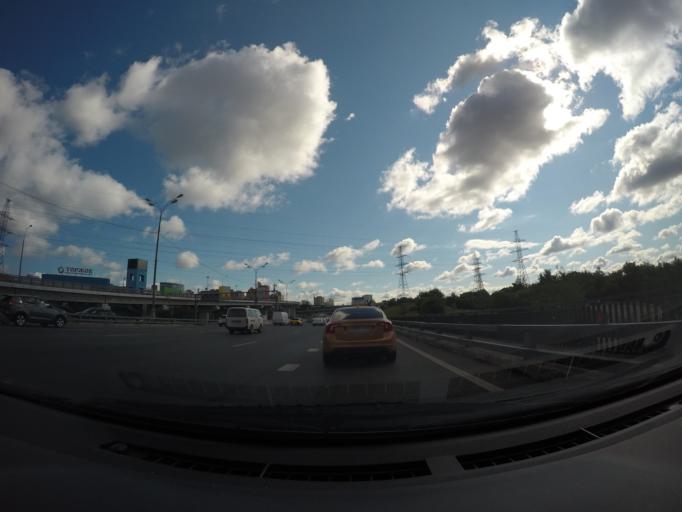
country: RU
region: Moscow
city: Khimki
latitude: 55.8798
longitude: 37.4346
